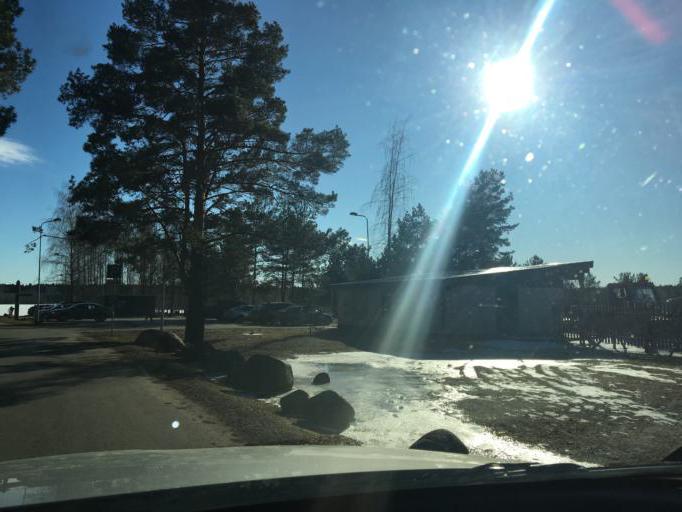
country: LV
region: Jekabpils Rajons
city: Jekabpils
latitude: 56.4831
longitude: 25.8522
